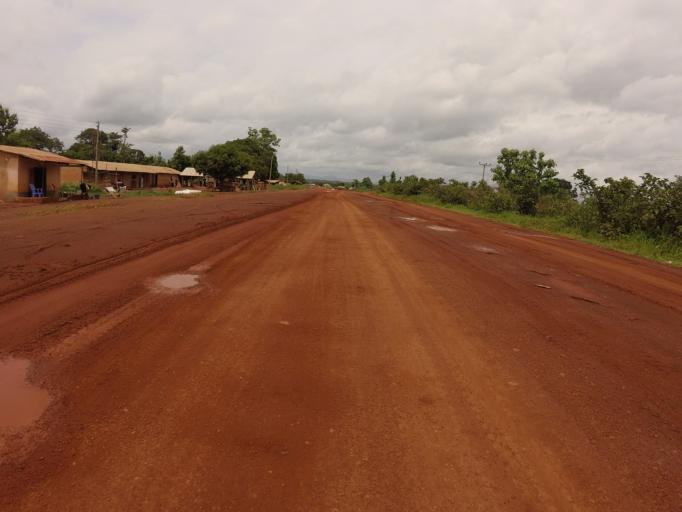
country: GH
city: Kpandae
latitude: 8.4047
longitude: 0.3996
